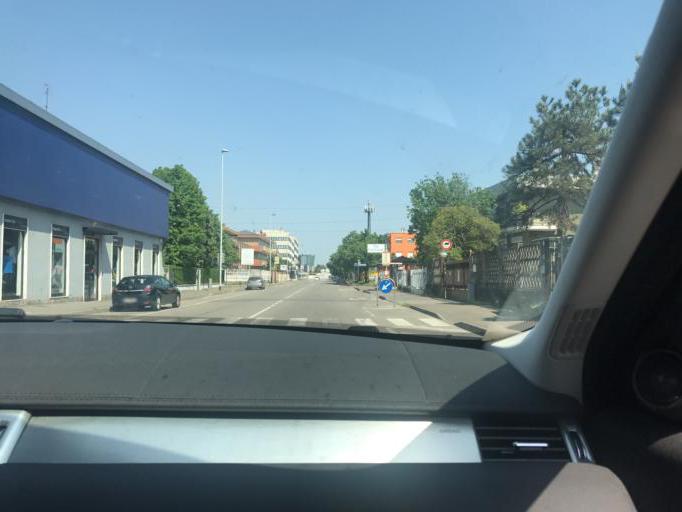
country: IT
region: Lombardy
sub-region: Citta metropolitana di Milano
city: Cesano Boscone
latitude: 45.4439
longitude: 9.1023
